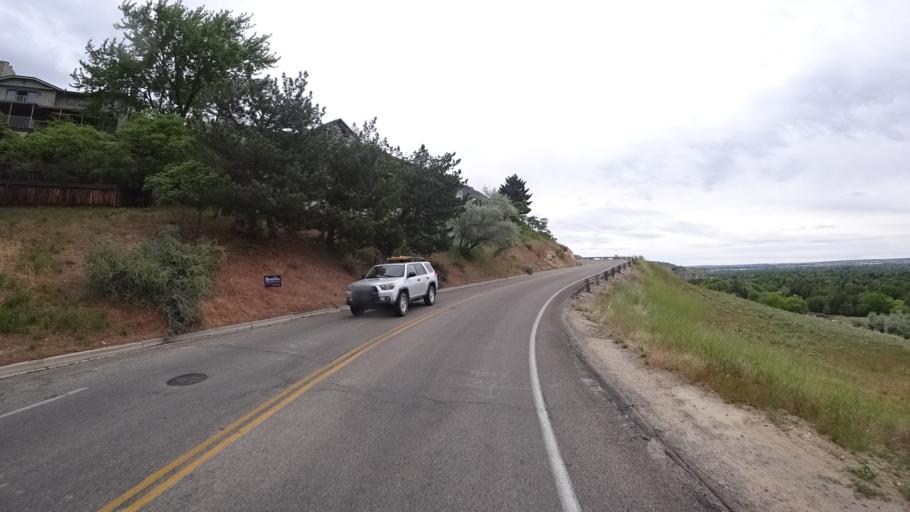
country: US
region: Idaho
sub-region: Ada County
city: Boise
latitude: 43.6154
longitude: -116.1769
